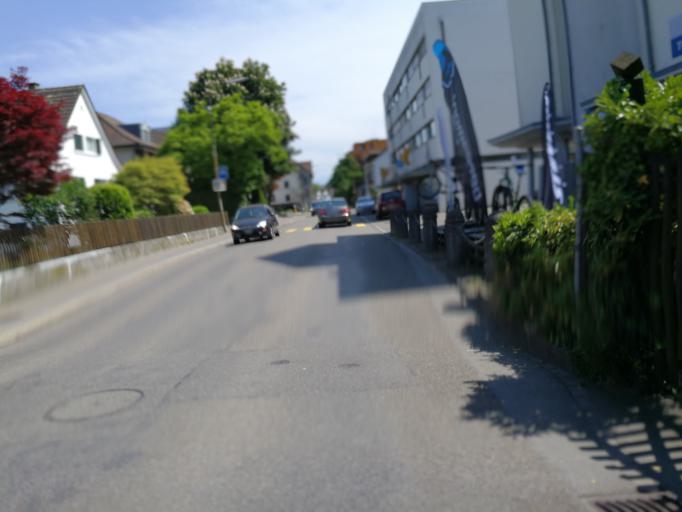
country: CH
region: Saint Gallen
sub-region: Wahlkreis See-Gaster
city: Rapperswil
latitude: 47.2294
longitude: 8.8280
